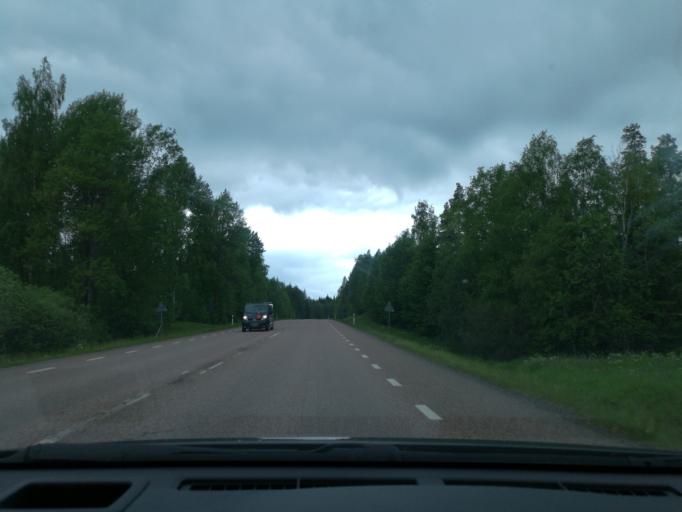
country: SE
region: Dalarna
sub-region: Smedjebackens Kommun
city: Smedjebacken
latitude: 60.1295
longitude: 15.4119
